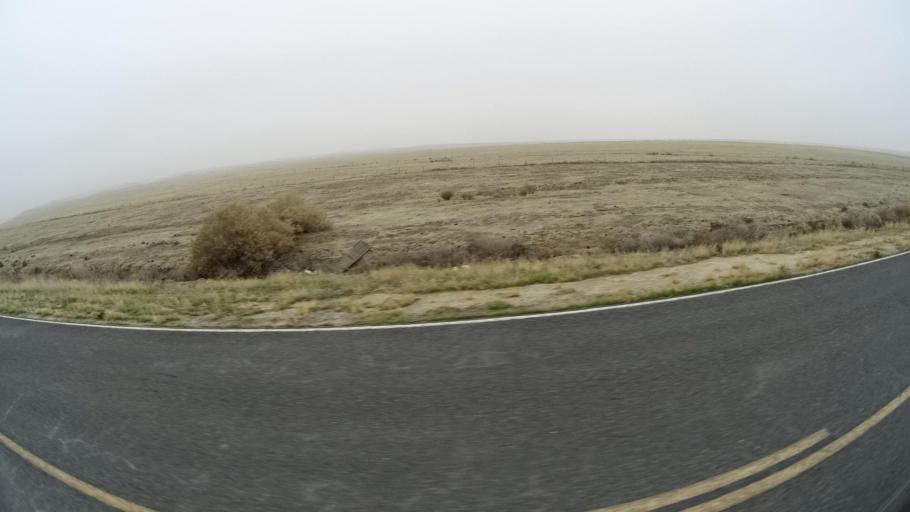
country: US
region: California
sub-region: Kern County
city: Buttonwillow
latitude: 35.3371
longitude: -119.4644
